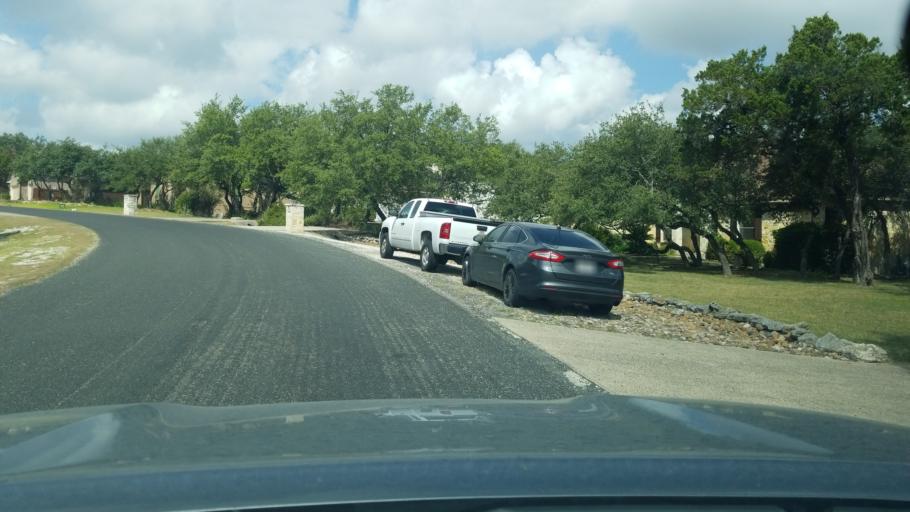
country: US
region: Texas
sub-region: Bexar County
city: Timberwood Park
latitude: 29.6925
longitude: -98.5091
